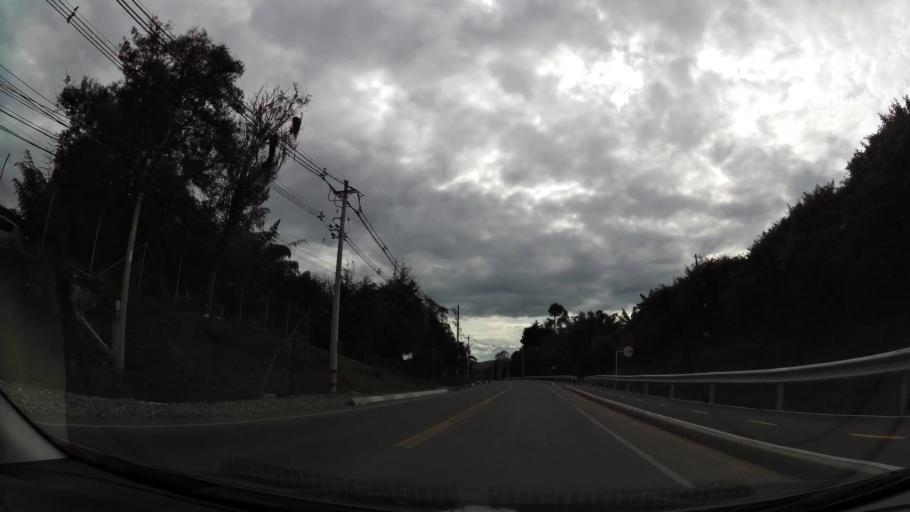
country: CO
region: Antioquia
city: Rionegro
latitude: 6.1506
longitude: -75.4168
